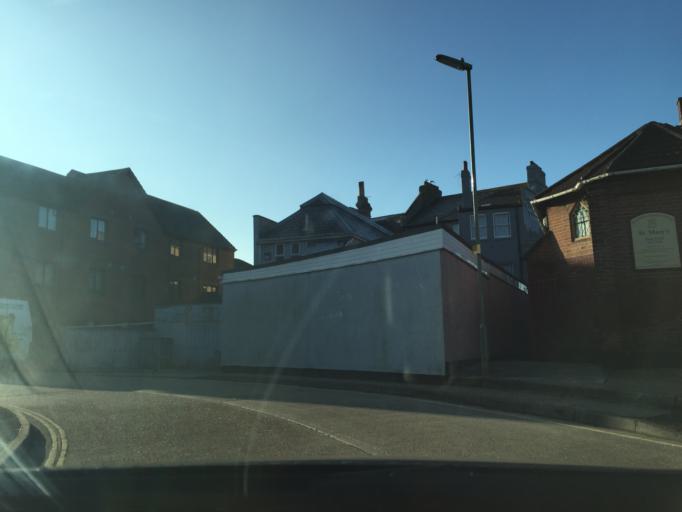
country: GB
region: England
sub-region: Hampshire
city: Gosport
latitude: 50.7959
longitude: -1.1216
